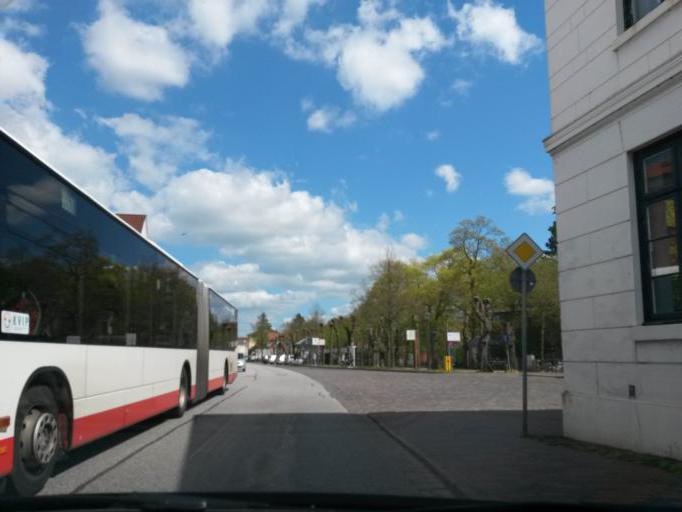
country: DE
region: Schleswig-Holstein
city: Uetersen
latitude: 53.6830
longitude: 9.6559
